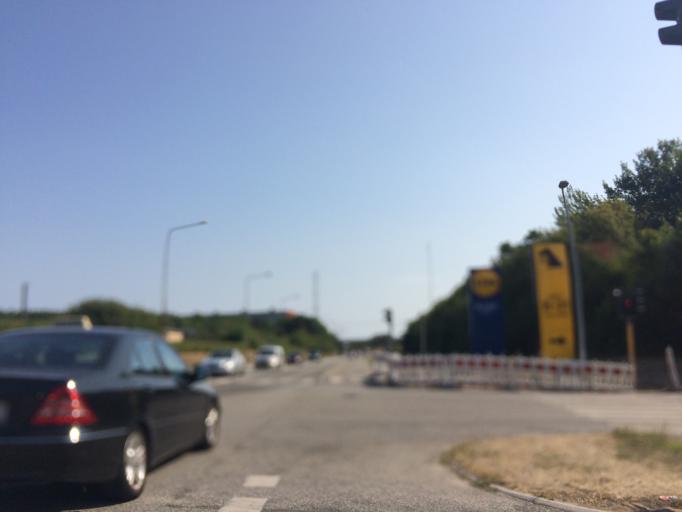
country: DK
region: Capital Region
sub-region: Hvidovre Kommune
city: Hvidovre
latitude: 55.6281
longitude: 12.4565
